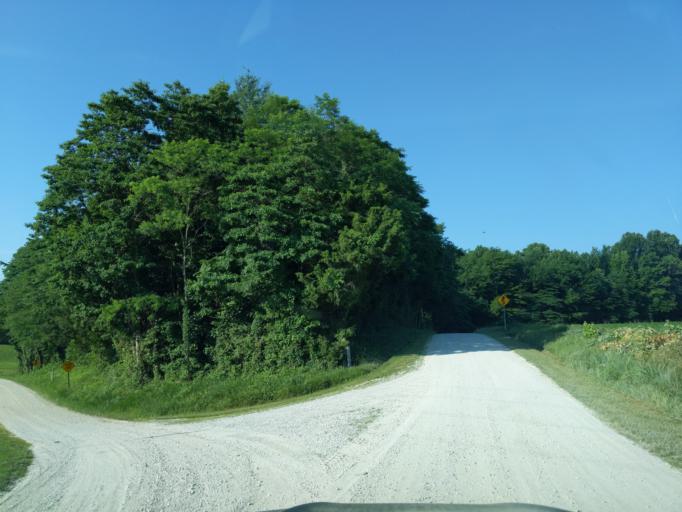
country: US
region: Indiana
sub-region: Decatur County
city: Westport
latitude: 39.2012
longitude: -85.4362
